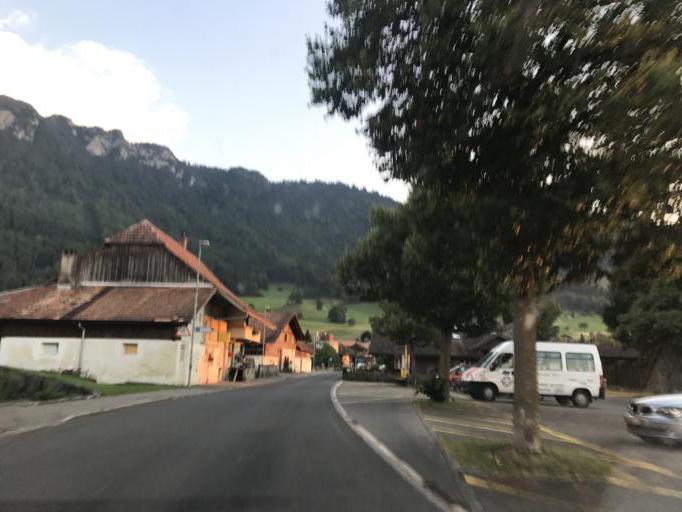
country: CH
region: Bern
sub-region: Frutigen-Niedersimmental District
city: Wimmis
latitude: 46.6966
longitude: 7.6240
